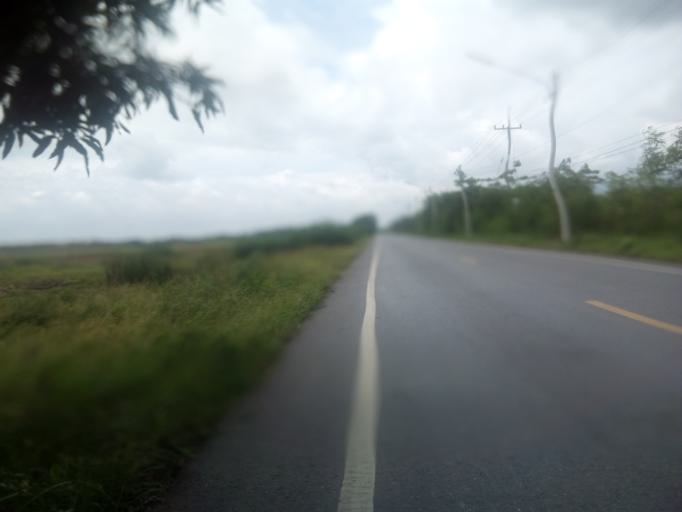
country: TH
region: Pathum Thani
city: Ban Lam Luk Ka
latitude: 14.0016
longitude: 100.8221
